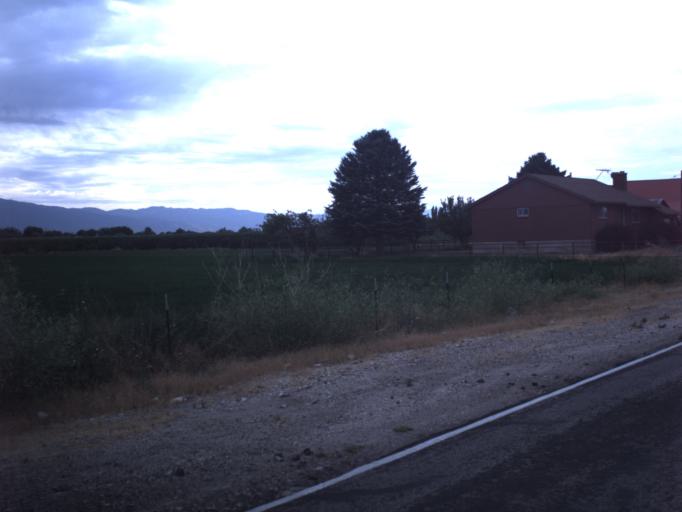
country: US
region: Utah
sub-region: Davis County
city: West Point
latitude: 41.1026
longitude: -112.1127
